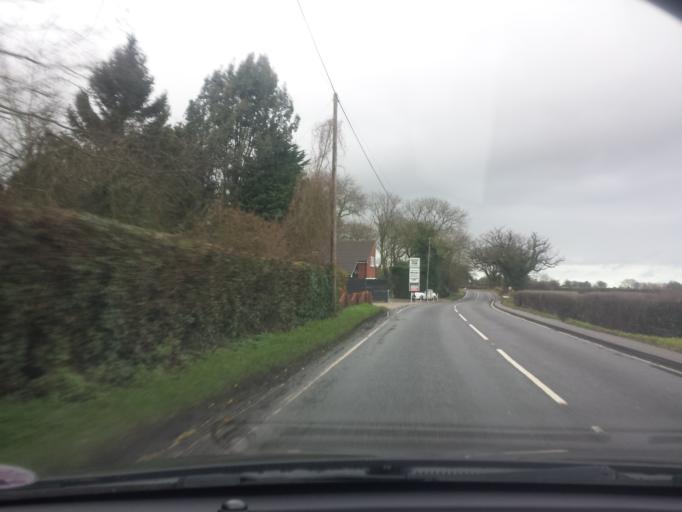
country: GB
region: England
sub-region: Essex
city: Great Bentley
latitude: 51.8847
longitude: 1.1103
